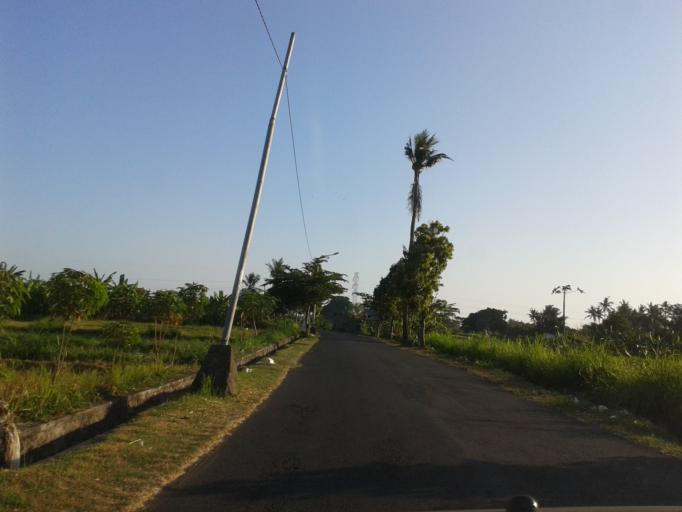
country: ID
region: Bali
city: Semarapura
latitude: -8.5596
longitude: 115.3868
